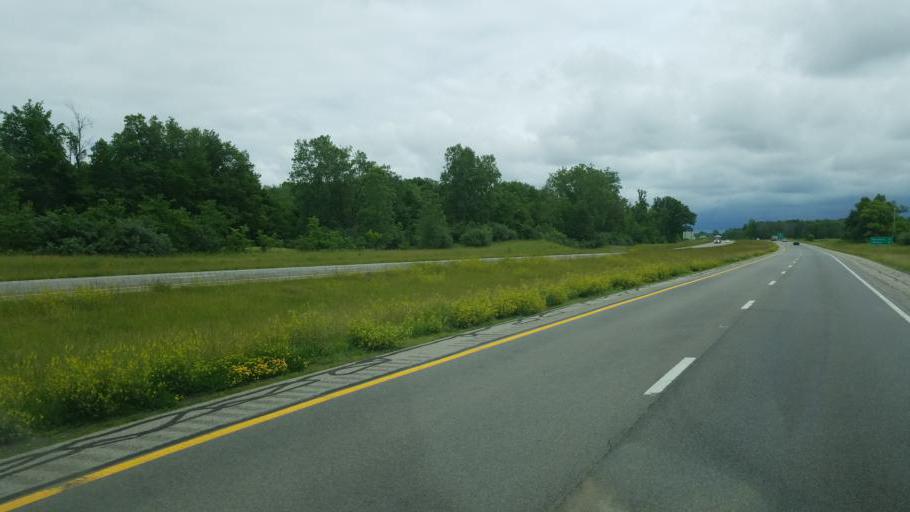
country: US
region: Ohio
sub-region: Crawford County
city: Galion
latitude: 40.7612
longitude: -82.7784
